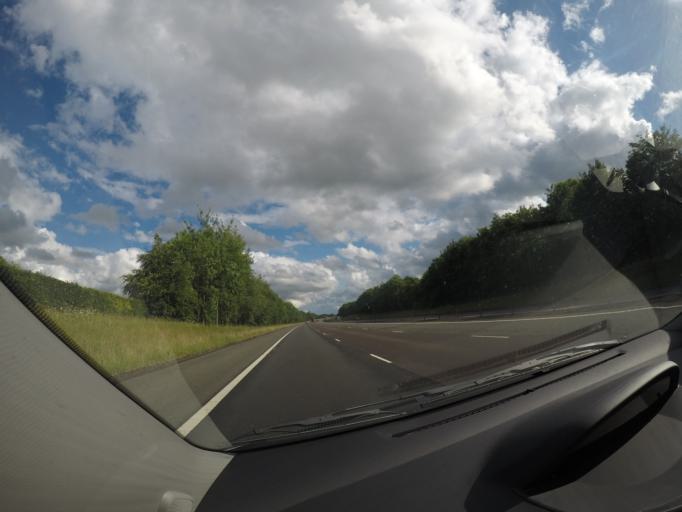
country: GB
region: Scotland
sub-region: Dumfries and Galloway
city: Moffat
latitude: 55.2530
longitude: -3.4105
